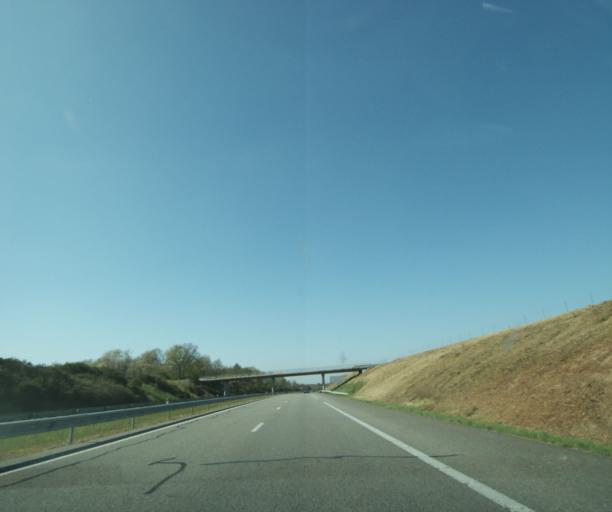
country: FR
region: Centre
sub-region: Departement du Loiret
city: Nogent-sur-Vernisson
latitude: 47.7424
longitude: 2.7276
